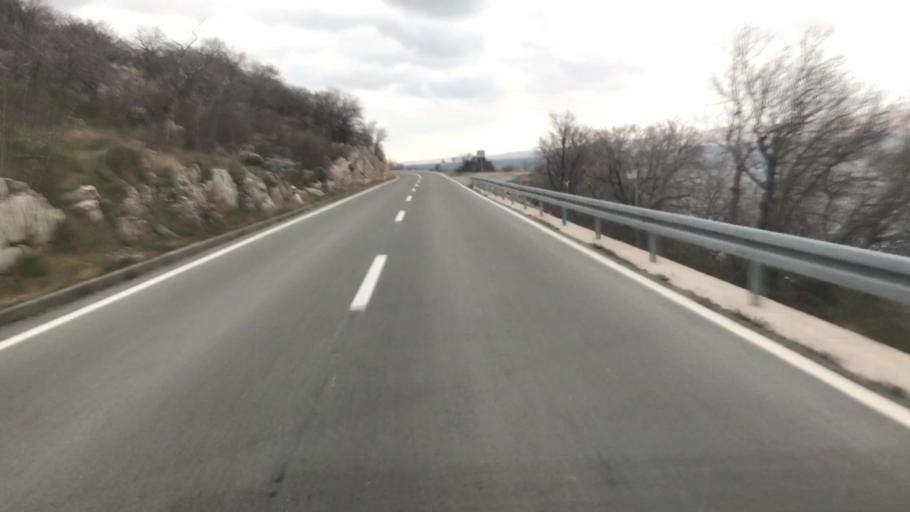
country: HR
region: Licko-Senjska
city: Karlobag
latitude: 44.5214
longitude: 15.0813
